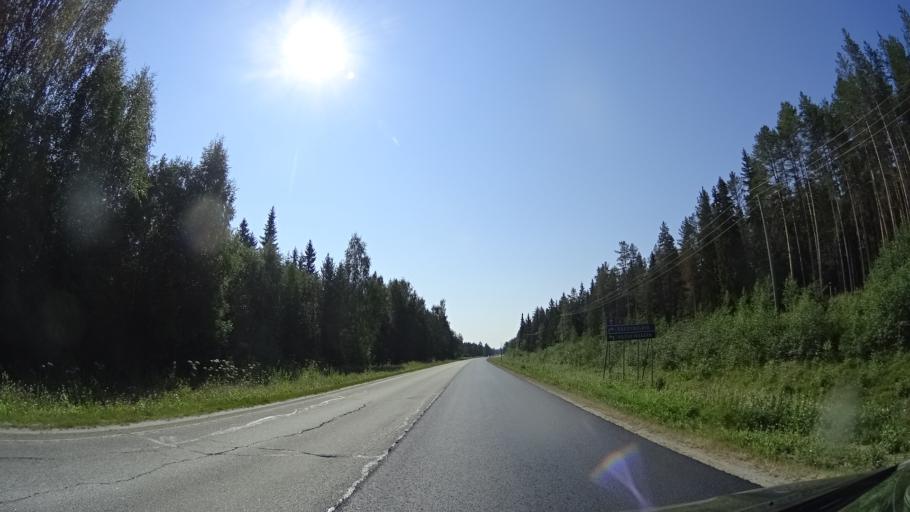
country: FI
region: North Karelia
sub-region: Joensuu
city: Juuka
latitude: 63.2203
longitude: 29.2988
